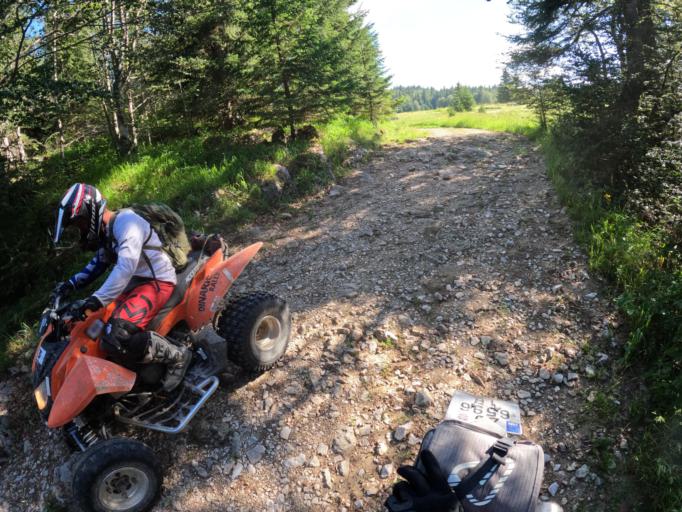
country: BA
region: Federation of Bosnia and Herzegovina
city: Glamoc
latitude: 44.1634
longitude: 16.9408
